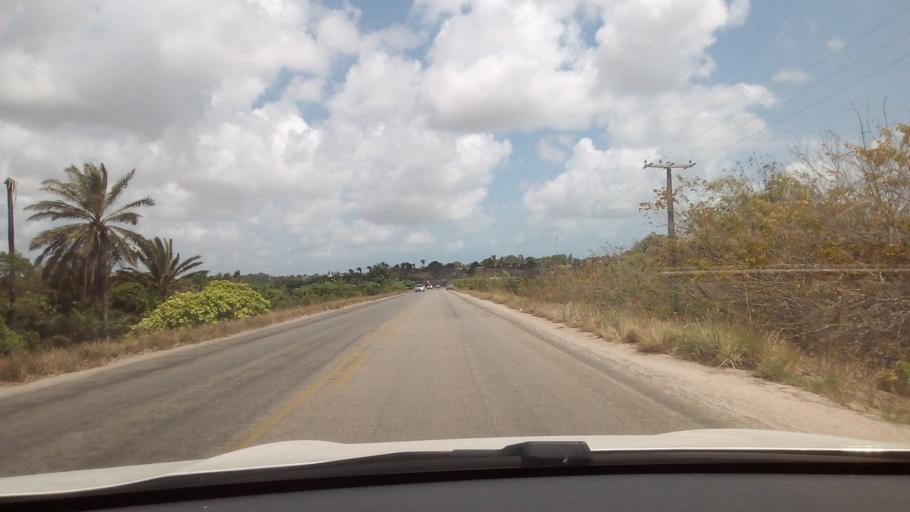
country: BR
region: Paraiba
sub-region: Conde
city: Conde
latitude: -7.2335
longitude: -34.8426
